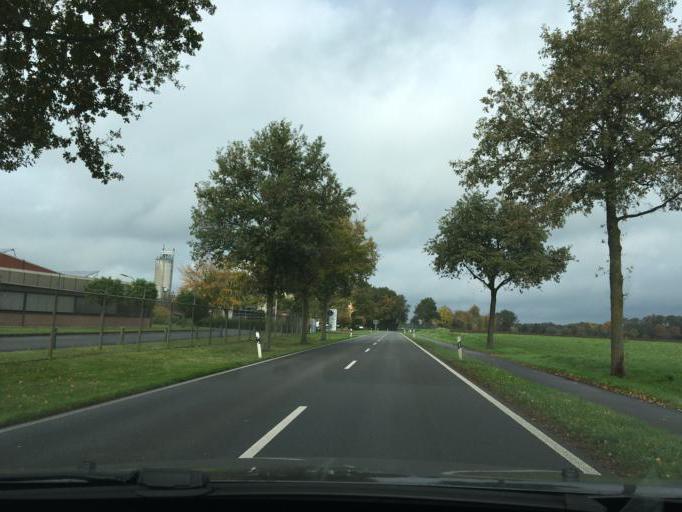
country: DE
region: North Rhine-Westphalia
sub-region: Regierungsbezirk Munster
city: Vreden
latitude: 52.0768
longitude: 6.7832
